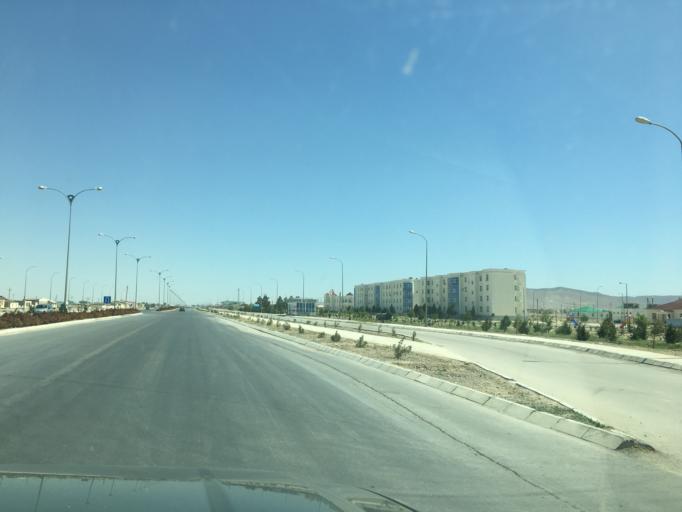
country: TM
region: Balkan
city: Serdar
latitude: 39.0003
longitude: 56.2653
